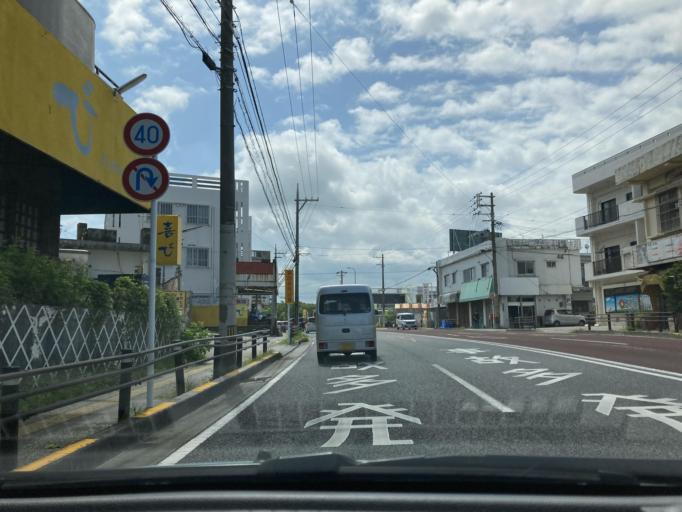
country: JP
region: Okinawa
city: Chatan
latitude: 26.2853
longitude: 127.7764
